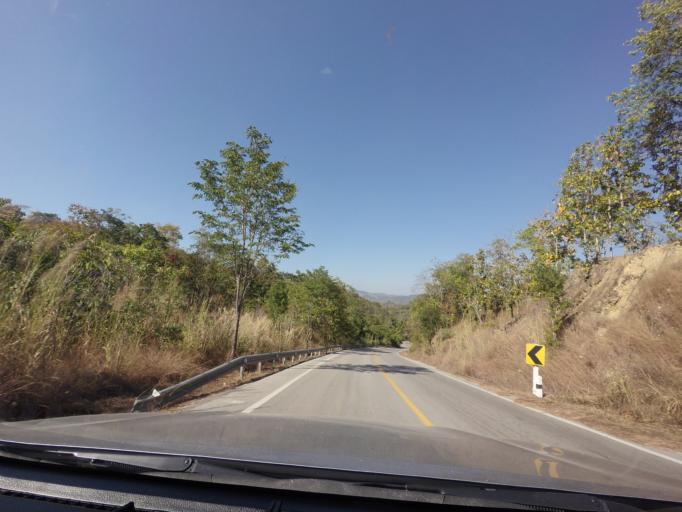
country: TH
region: Lampang
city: Chae Hom
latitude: 18.5752
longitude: 99.6270
